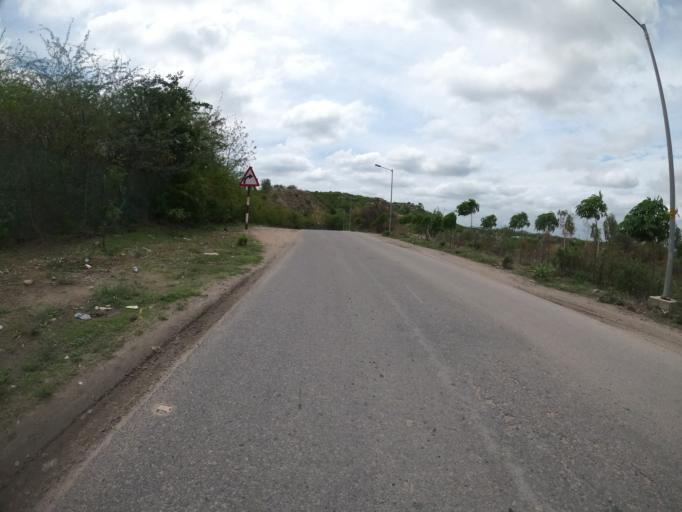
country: IN
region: Telangana
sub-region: Hyderabad
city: Hyderabad
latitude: 17.3122
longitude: 78.3742
